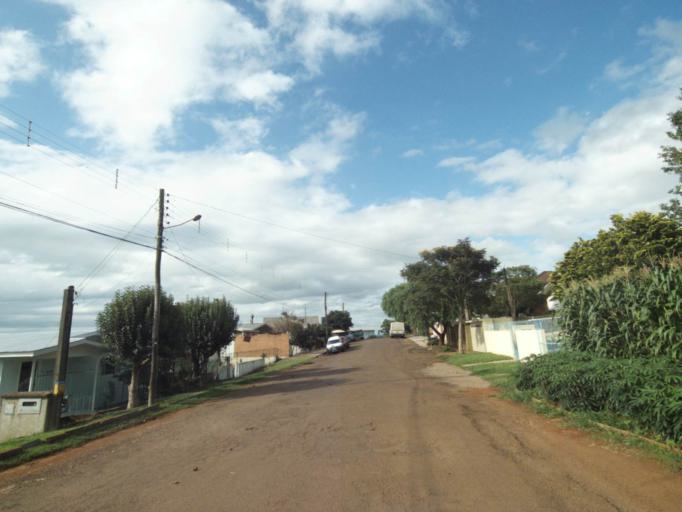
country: BR
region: Rio Grande do Sul
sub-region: Lagoa Vermelha
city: Lagoa Vermelha
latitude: -28.2040
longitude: -51.5190
